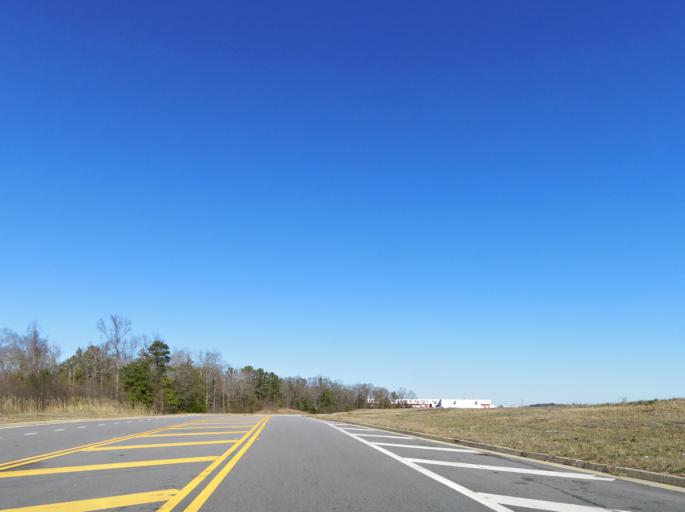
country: US
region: Georgia
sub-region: Peach County
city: Byron
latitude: 32.7171
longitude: -83.7349
